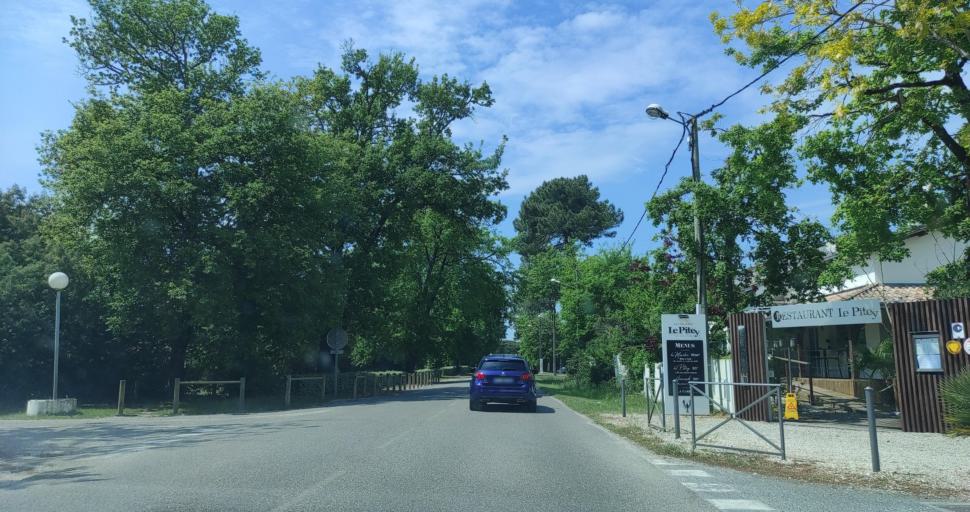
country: FR
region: Aquitaine
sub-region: Departement de la Gironde
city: Ares
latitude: 44.7602
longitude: -1.1251
